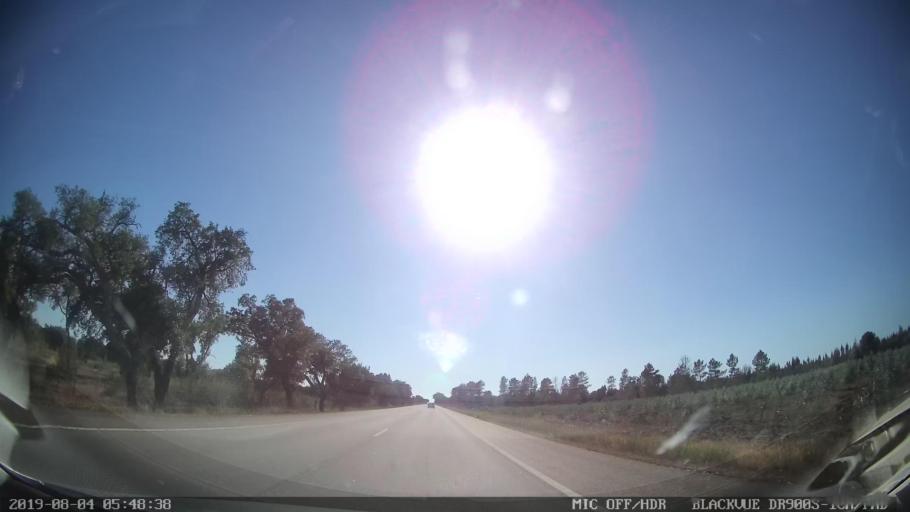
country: PT
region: Portalegre
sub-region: Gaviao
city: Gaviao
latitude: 39.4443
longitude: -7.8305
